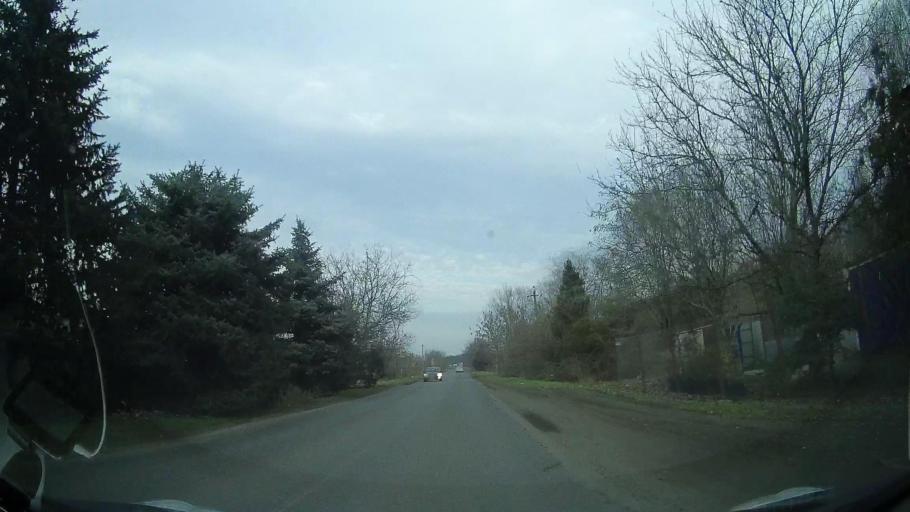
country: RU
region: Rostov
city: Ol'ginskaya
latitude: 47.1325
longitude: 39.8867
